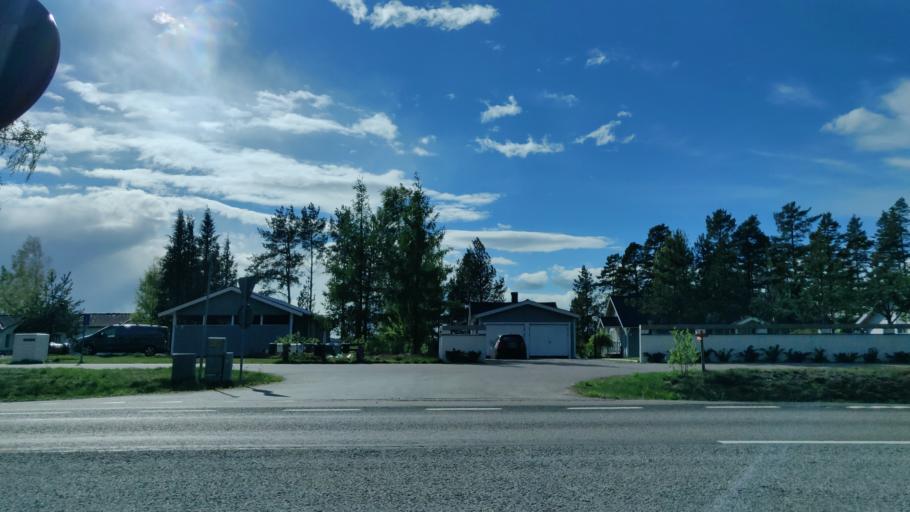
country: SE
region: Vaermland
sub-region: Forshaga Kommun
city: Forshaga
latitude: 59.4770
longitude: 13.4107
